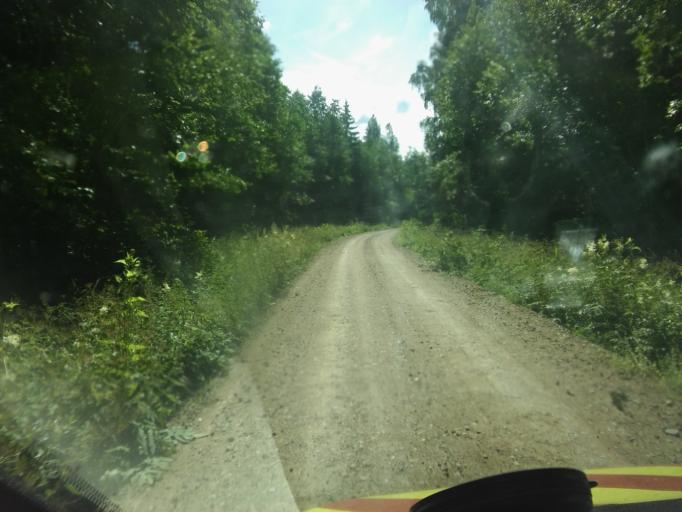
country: EE
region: Paernumaa
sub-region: Paikuse vald
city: Paikuse
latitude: 58.2905
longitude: 24.6959
